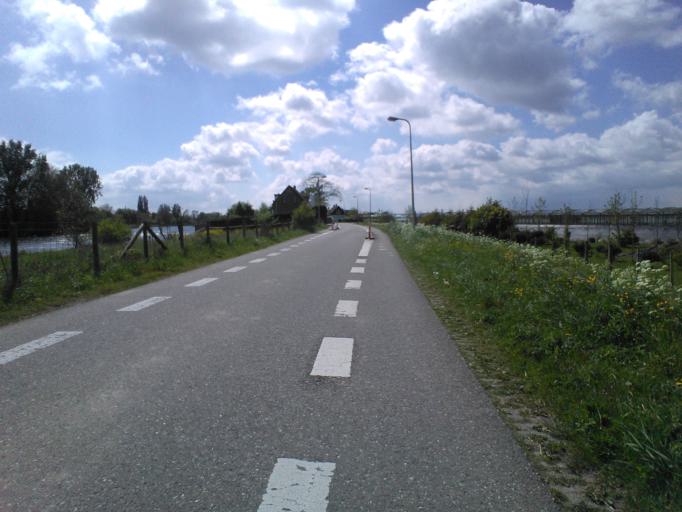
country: NL
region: South Holland
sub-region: Gemeente Hendrik-Ido-Ambacht
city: Hendrik-Ido-Ambacht
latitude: 51.8545
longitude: 4.6248
